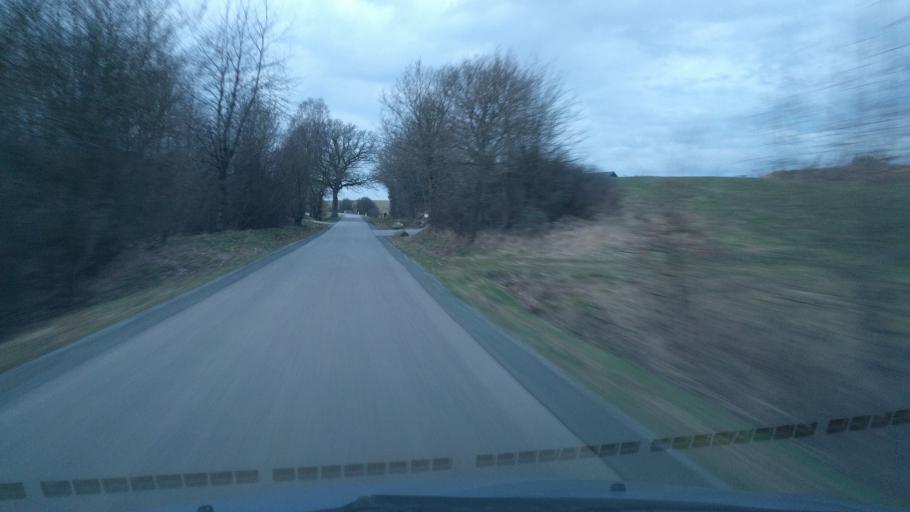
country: DK
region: South Denmark
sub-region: Haderslev Kommune
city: Haderslev
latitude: 55.2572
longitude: 9.4296
